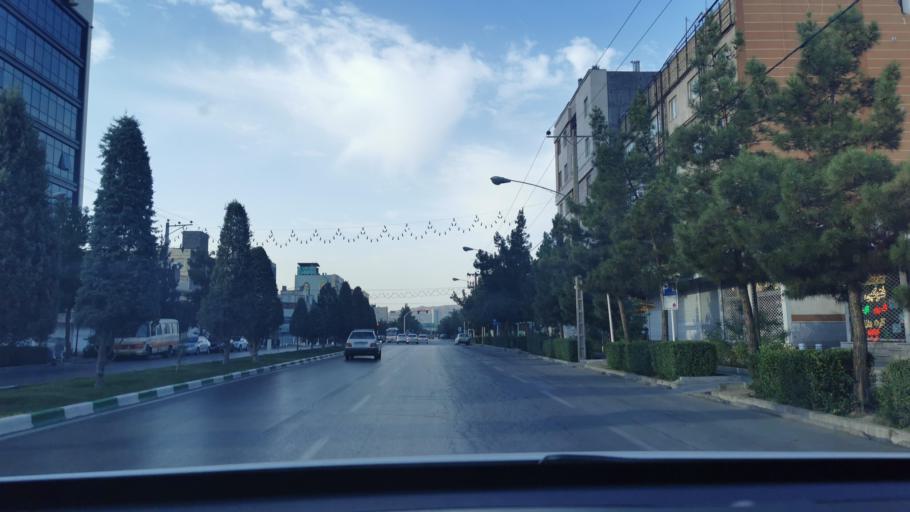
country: IR
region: Razavi Khorasan
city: Mashhad
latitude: 36.3533
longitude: 59.5016
